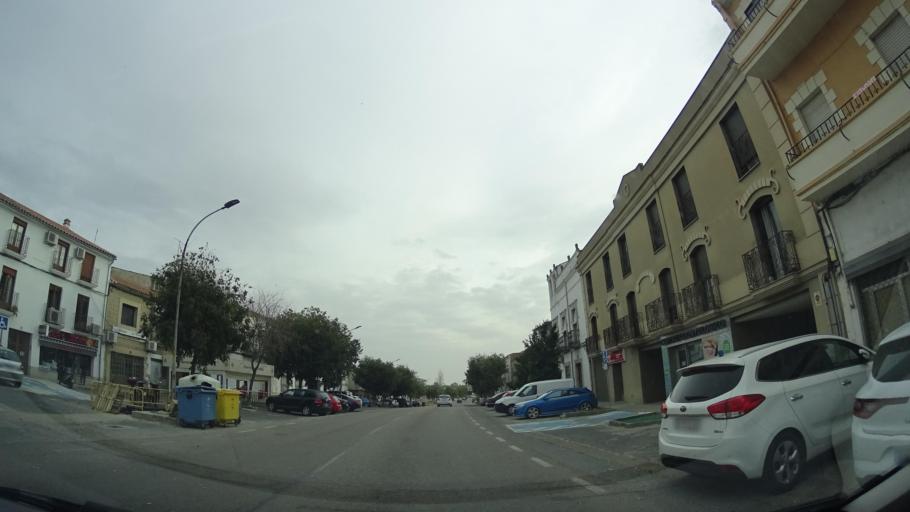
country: ES
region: Extremadura
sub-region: Provincia de Caceres
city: Trujillo
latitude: 39.4559
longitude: -5.8813
